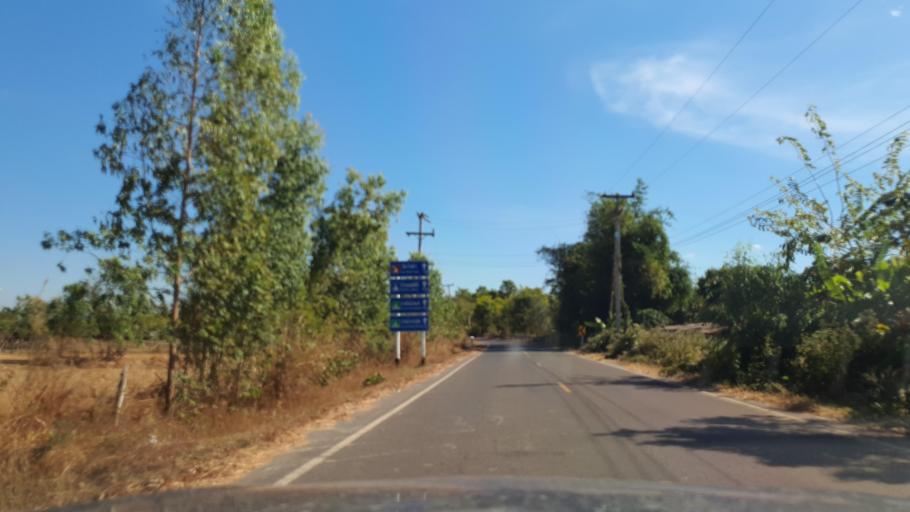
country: TH
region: Kalasin
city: Khao Wong
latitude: 16.6872
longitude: 104.1157
